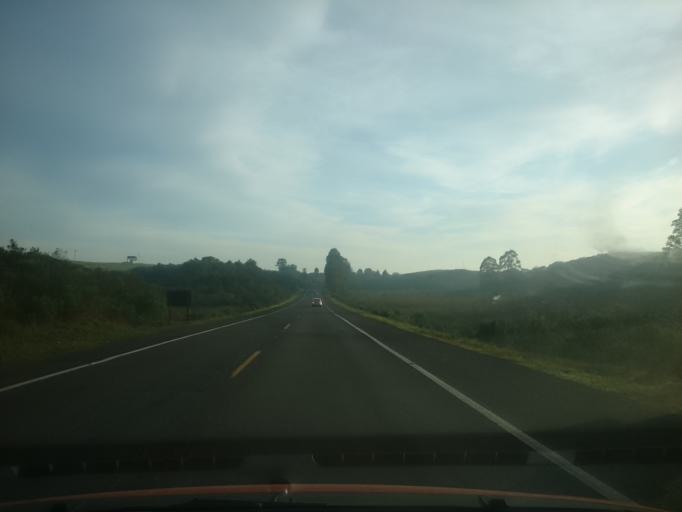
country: BR
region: Rio Grande do Sul
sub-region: Vacaria
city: Vacaria
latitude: -28.3185
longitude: -50.8047
